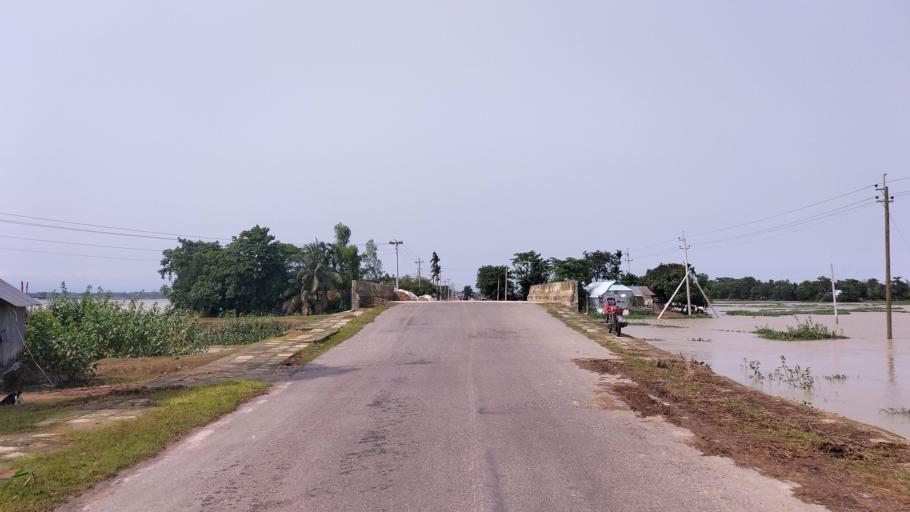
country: BD
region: Dhaka
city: Netrakona
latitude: 25.0161
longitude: 90.8554
